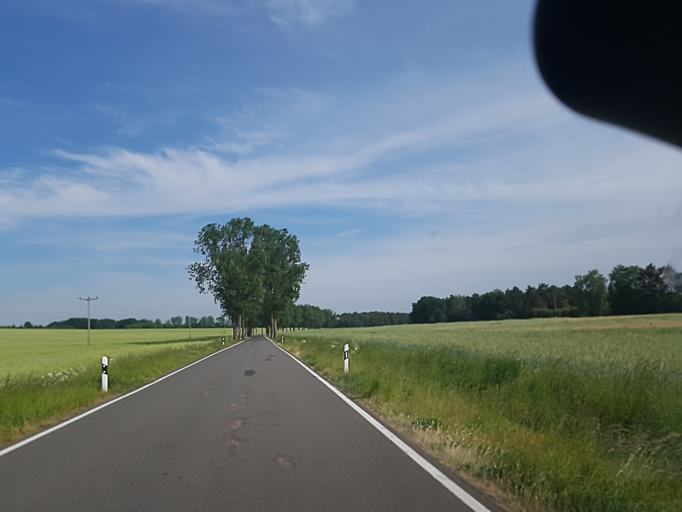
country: DE
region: Saxony-Anhalt
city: Kropstadt
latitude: 51.9740
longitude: 12.7295
